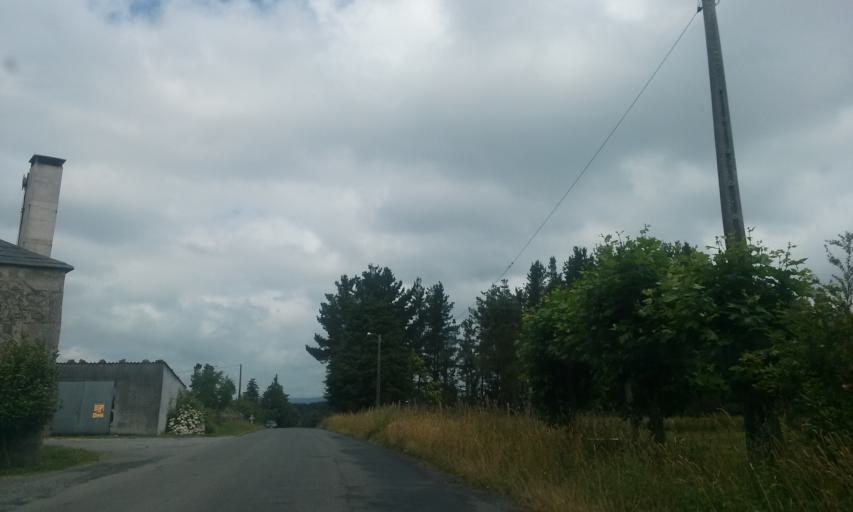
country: ES
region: Galicia
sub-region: Provincia de Lugo
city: Friol
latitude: 43.0875
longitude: -7.8098
